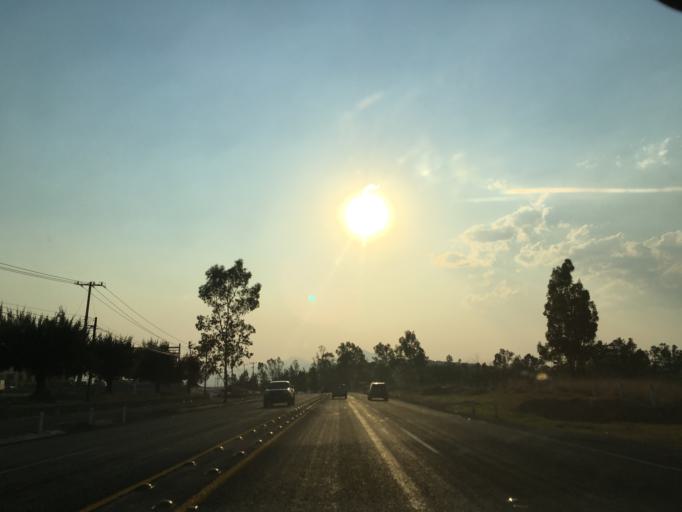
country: MX
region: Michoacan
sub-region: Morelia
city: La Aldea
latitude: 19.7344
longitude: -101.1270
